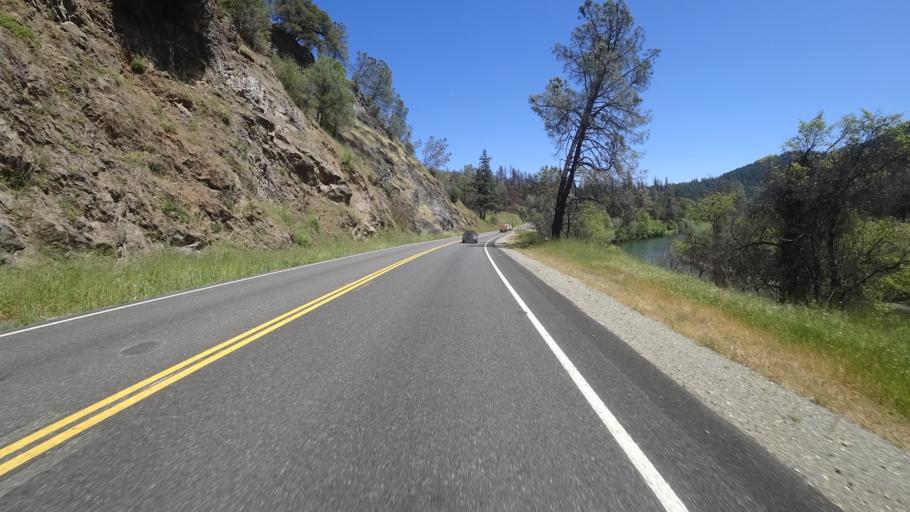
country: US
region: California
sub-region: Trinity County
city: Weaverville
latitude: 40.7664
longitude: -123.1058
